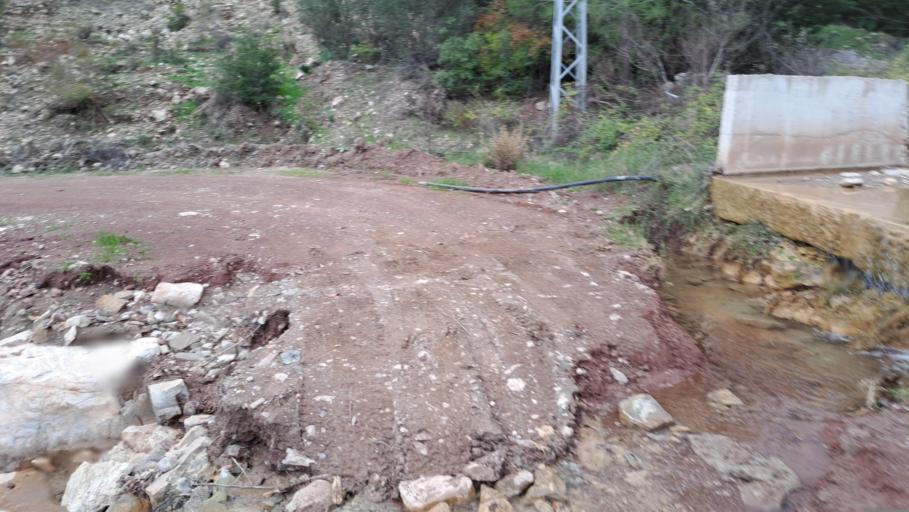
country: TR
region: Antalya
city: Tekirova
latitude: 36.4001
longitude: 30.4290
